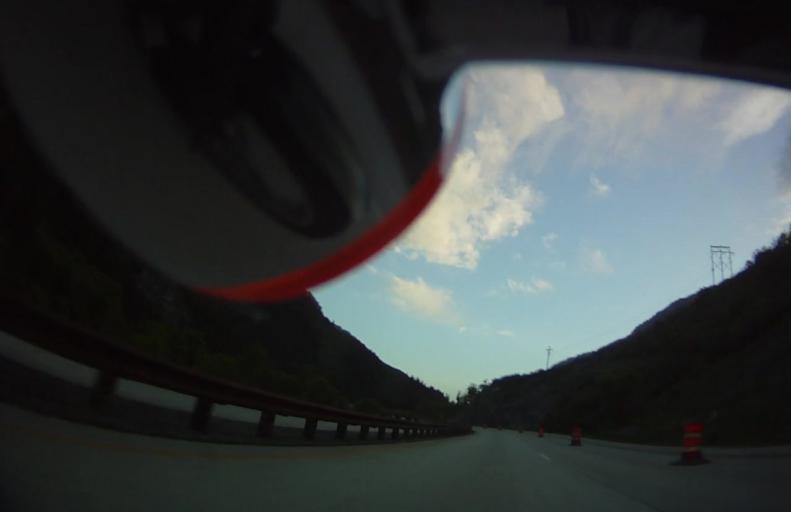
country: US
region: Utah
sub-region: Utah County
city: Orem
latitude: 40.3591
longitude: -111.5681
